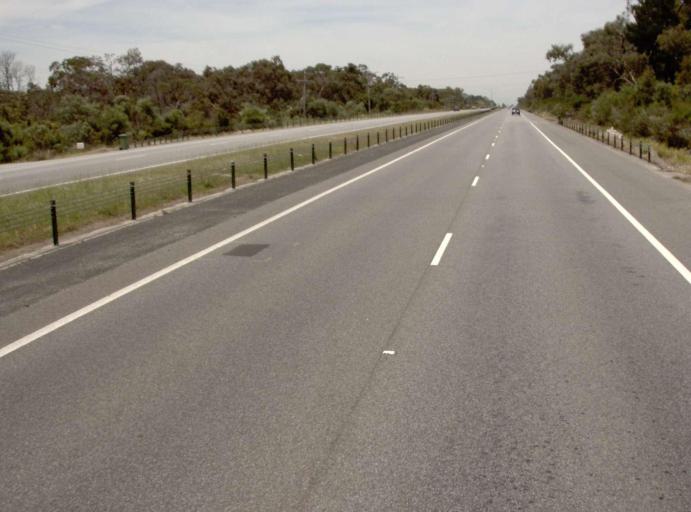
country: AU
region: Victoria
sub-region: Casey
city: Cranbourne South
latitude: -38.1467
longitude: 145.2257
